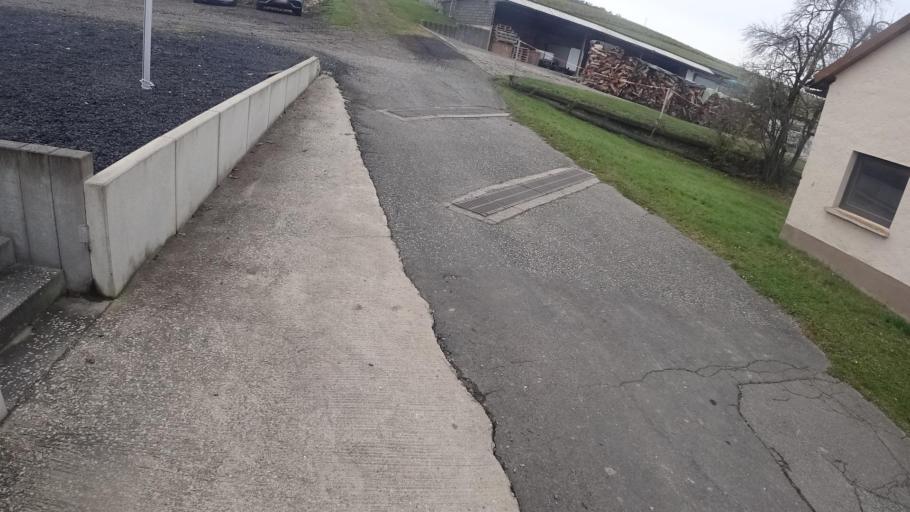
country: DE
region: Rheinland-Pfalz
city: Thorlingen
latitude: 50.1333
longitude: 7.5326
